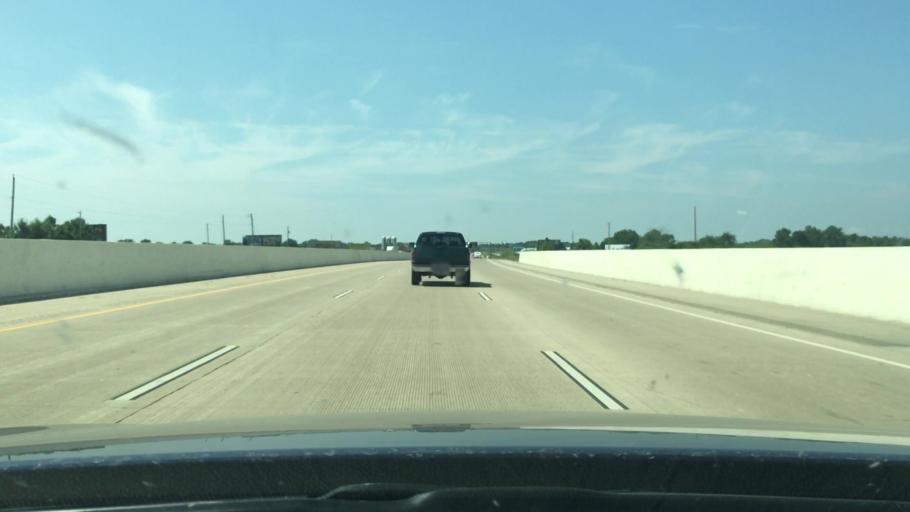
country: US
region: Wisconsin
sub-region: Winnebago County
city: Neenah
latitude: 44.1211
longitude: -88.5056
